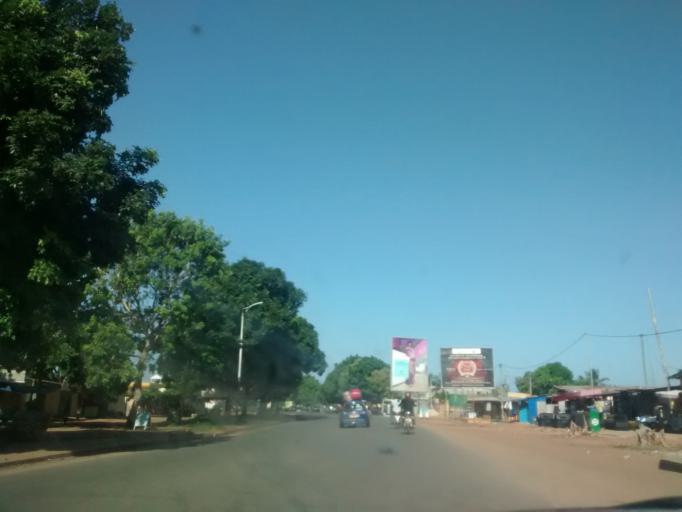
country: TG
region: Maritime
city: Lome
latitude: 6.1708
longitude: 1.1916
